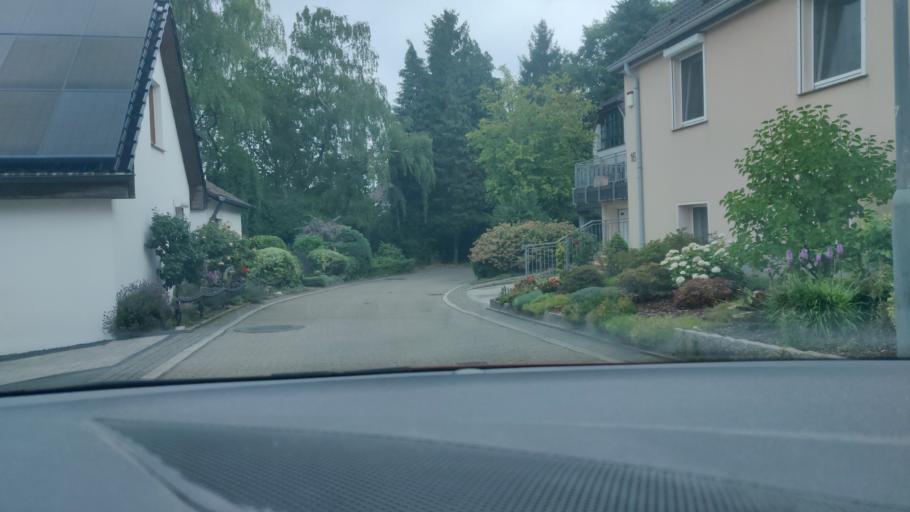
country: DE
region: North Rhine-Westphalia
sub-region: Regierungsbezirk Dusseldorf
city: Velbert
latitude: 51.3537
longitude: 7.0305
